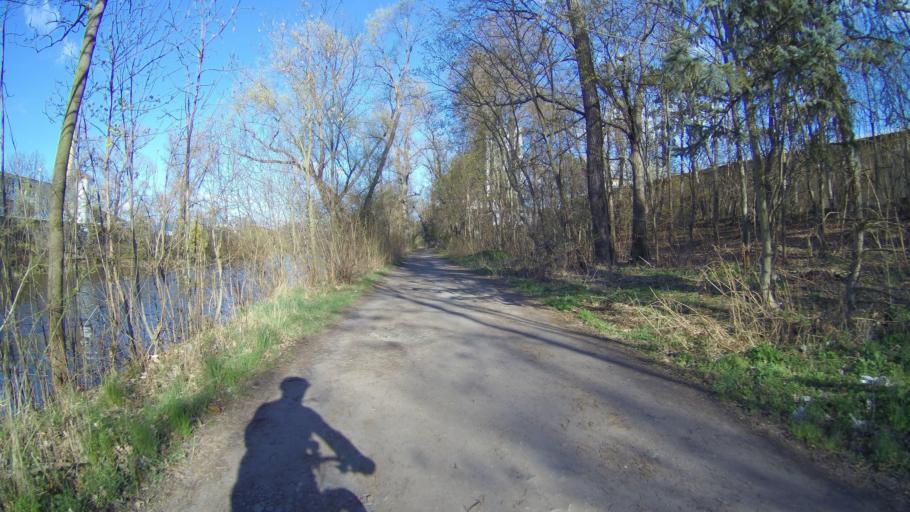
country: CZ
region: Ustecky
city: Zatec
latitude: 50.3324
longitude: 13.5548
